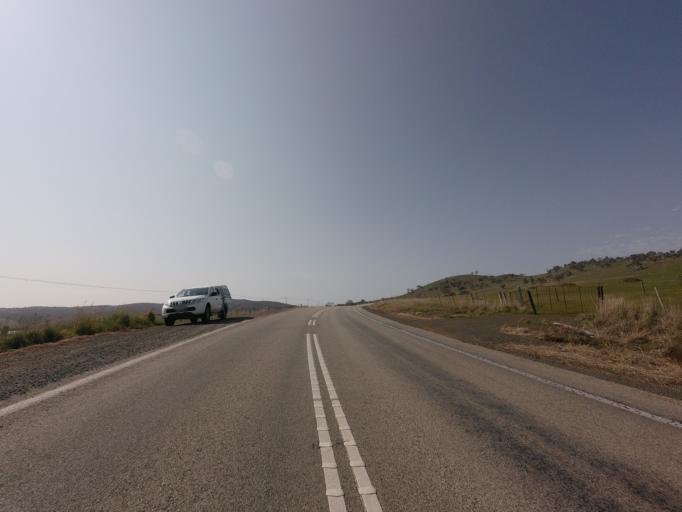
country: AU
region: Tasmania
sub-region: Northern Midlands
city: Evandale
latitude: -41.8221
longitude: 147.5254
